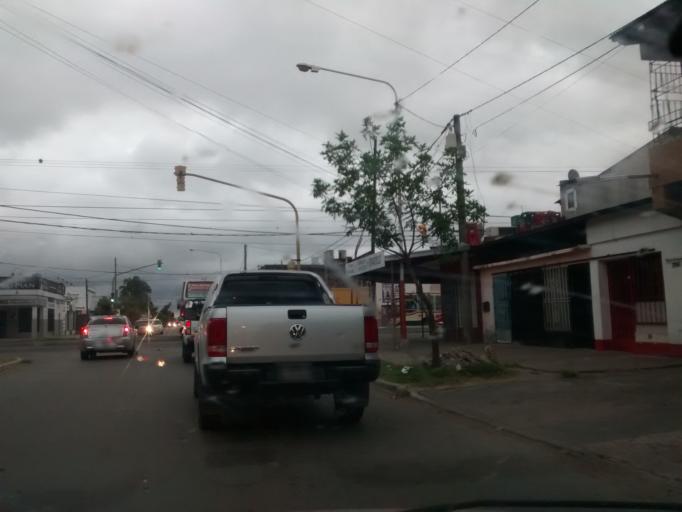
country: AR
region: Chaco
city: Resistencia
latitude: -27.4485
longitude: -59.0032
